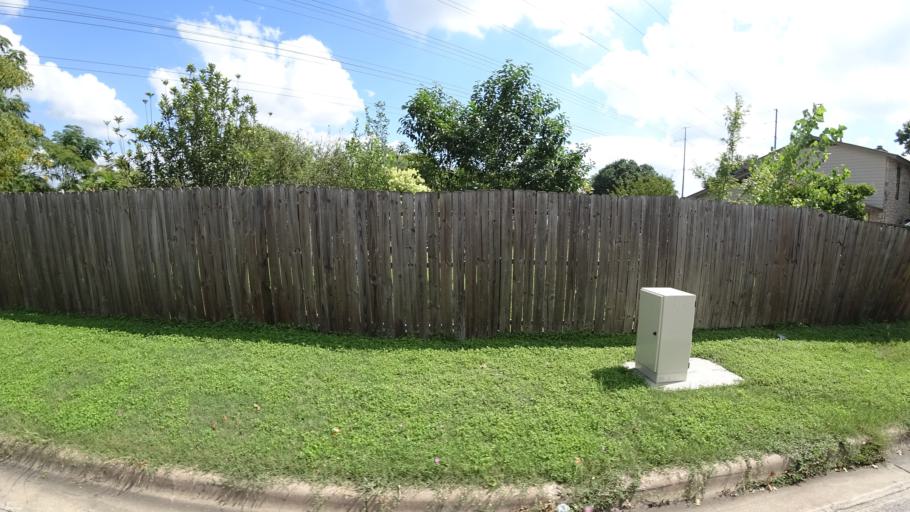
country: US
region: Texas
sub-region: Travis County
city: Onion Creek
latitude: 30.1941
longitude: -97.7834
